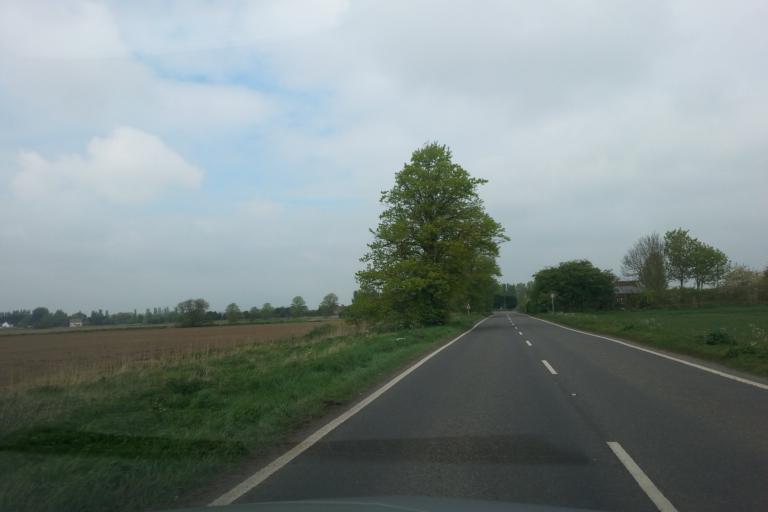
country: GB
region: England
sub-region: Norfolk
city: Outwell
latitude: 52.5684
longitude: 0.2290
